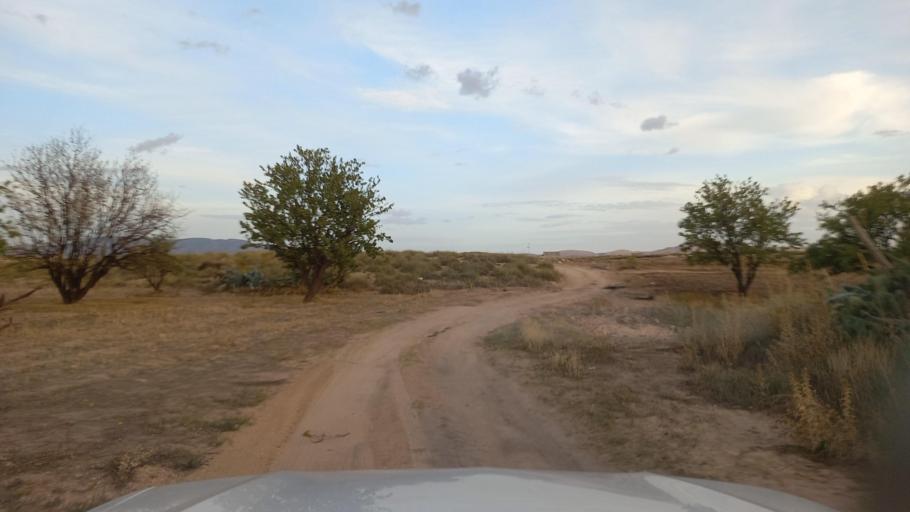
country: TN
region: Al Qasrayn
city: Sbiba
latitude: 35.4097
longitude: 9.0862
